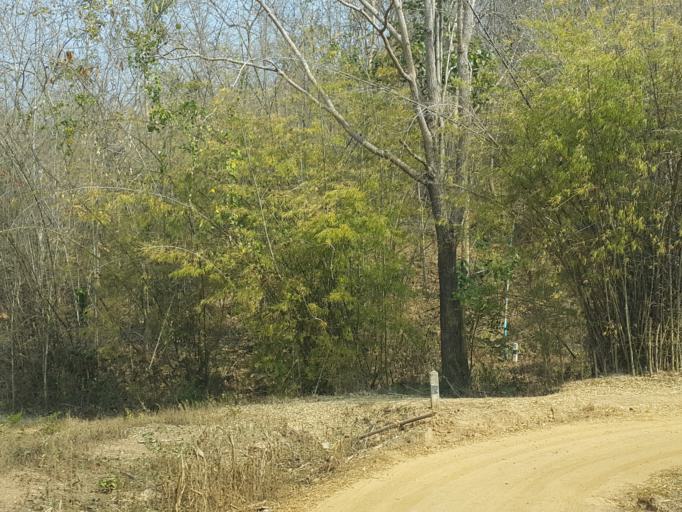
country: TH
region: Chiang Mai
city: Hang Dong
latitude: 18.7367
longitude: 98.8598
